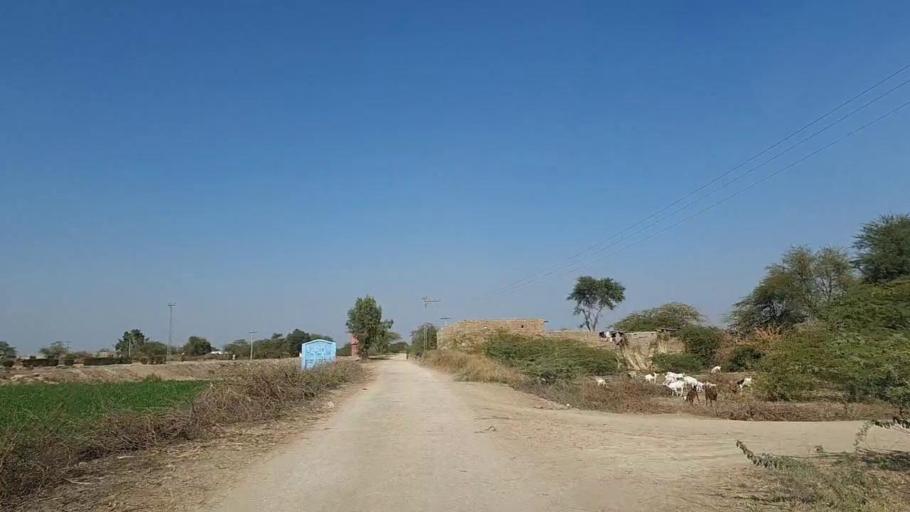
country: PK
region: Sindh
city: Nawabshah
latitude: 26.2529
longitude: 68.4411
